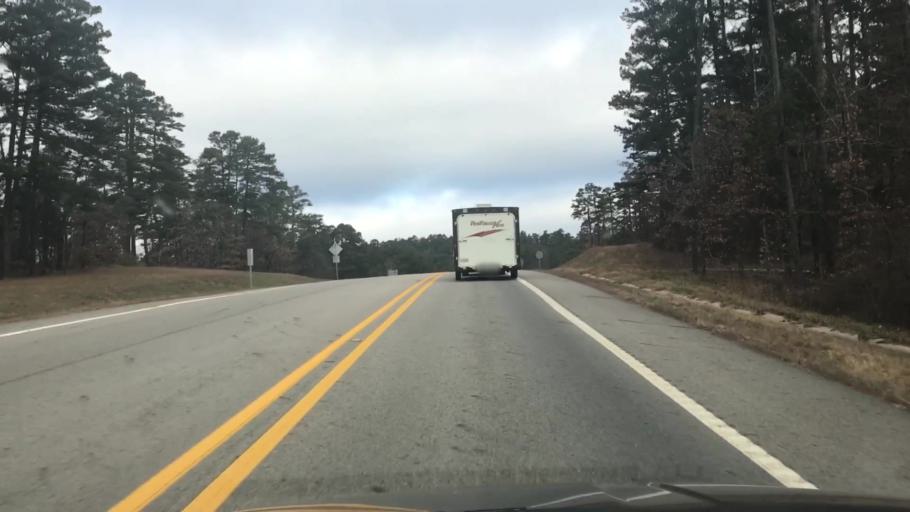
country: US
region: Arkansas
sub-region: Montgomery County
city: Mount Ida
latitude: 34.6802
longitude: -93.7877
